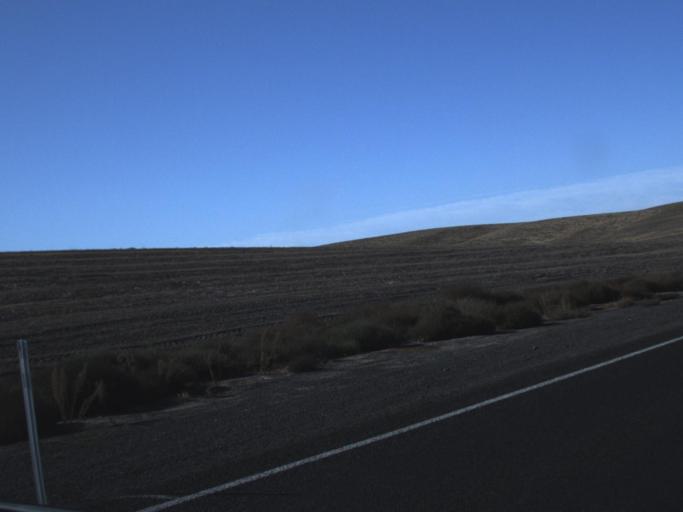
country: US
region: Washington
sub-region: Walla Walla County
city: Walla Walla
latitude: 46.1269
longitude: -118.3742
